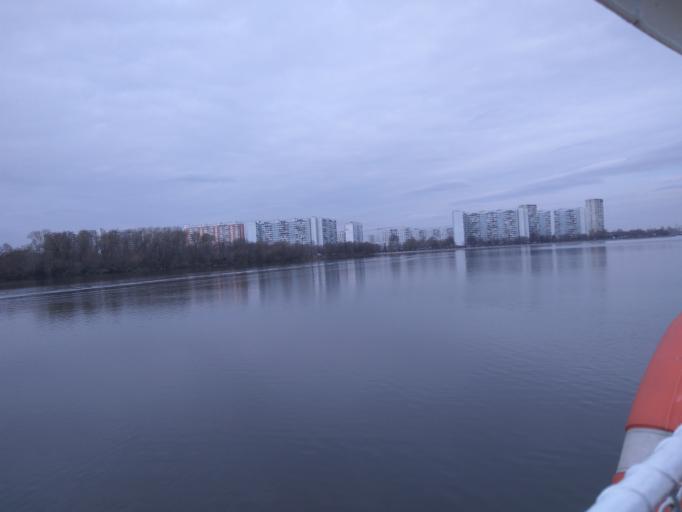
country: RU
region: Moscow
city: Mar'ino
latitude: 55.6759
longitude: 37.7143
